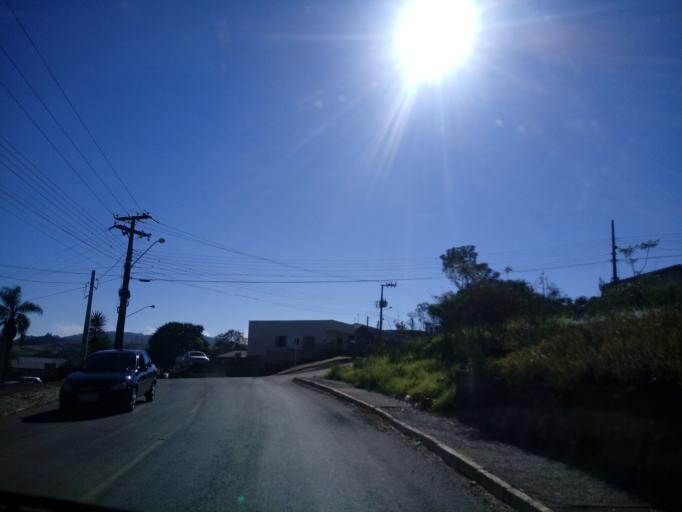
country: BR
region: Santa Catarina
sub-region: Chapeco
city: Chapeco
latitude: -27.0674
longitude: -52.6065
